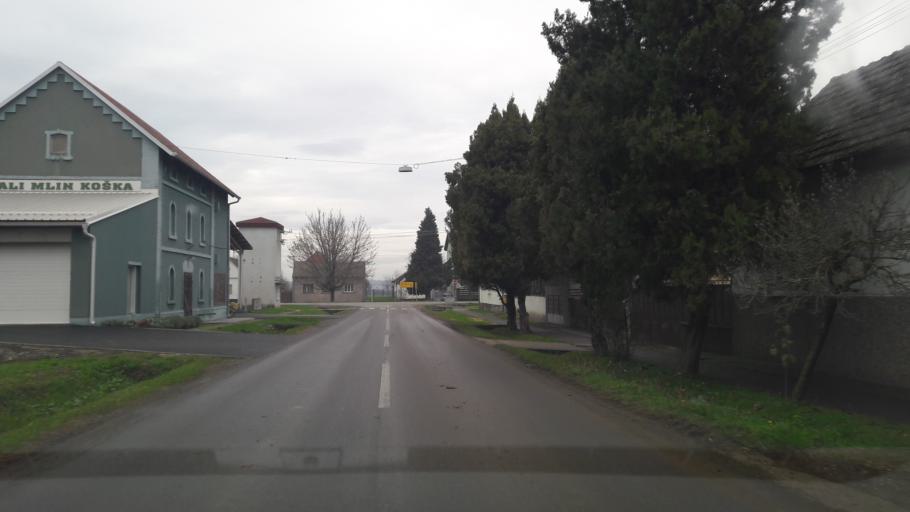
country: HR
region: Osjecko-Baranjska
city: Koska
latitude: 45.5441
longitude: 18.2918
